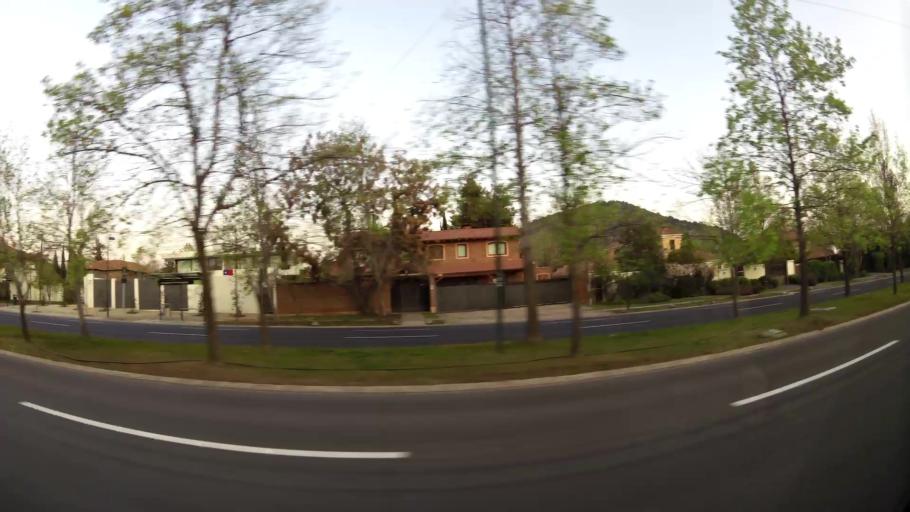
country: CL
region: Santiago Metropolitan
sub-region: Provincia de Chacabuco
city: Chicureo Abajo
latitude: -33.3346
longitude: -70.5440
